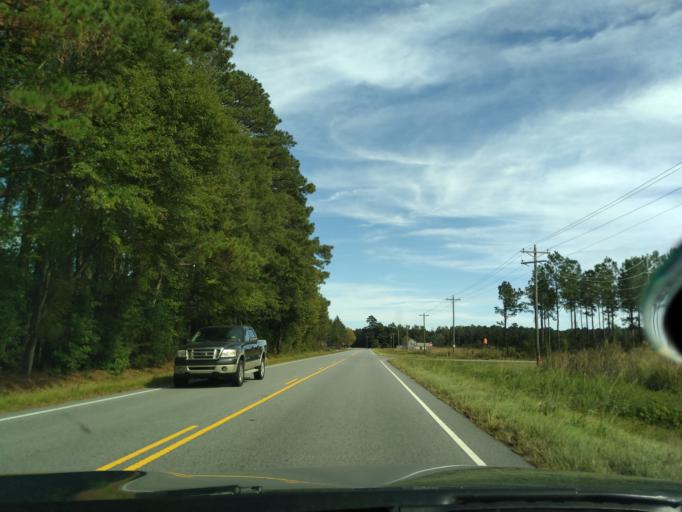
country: US
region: North Carolina
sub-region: Beaufort County
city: River Road
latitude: 35.5215
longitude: -76.8277
